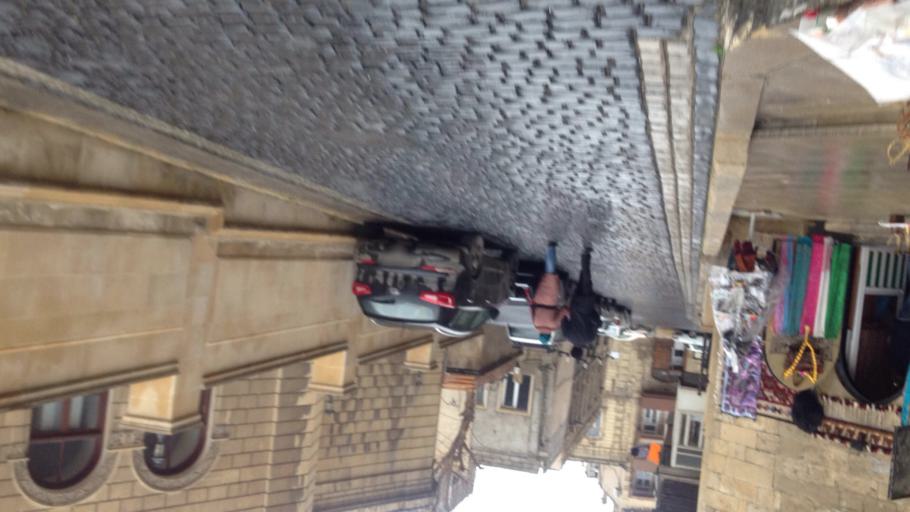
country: AZ
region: Baki
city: Badamdar
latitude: 40.3652
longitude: 49.8356
